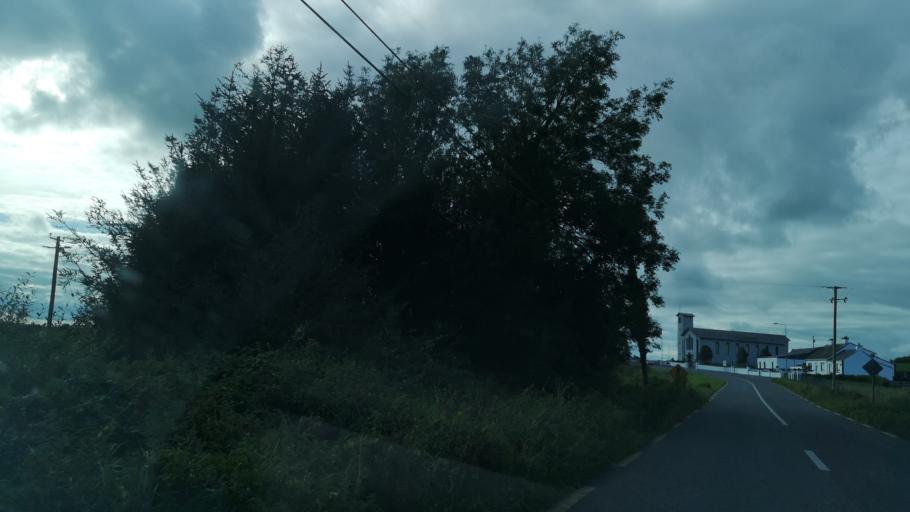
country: IE
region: Connaught
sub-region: County Galway
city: Ballinasloe
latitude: 53.2942
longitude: -8.0997
